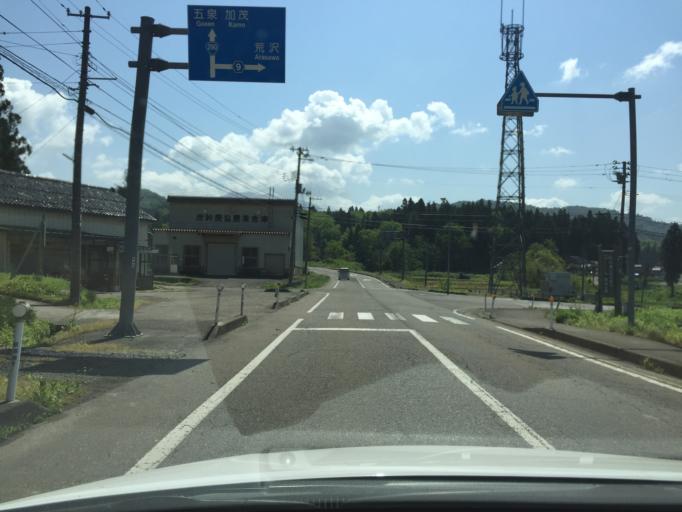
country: JP
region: Niigata
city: Kamo
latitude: 37.5759
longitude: 139.0864
